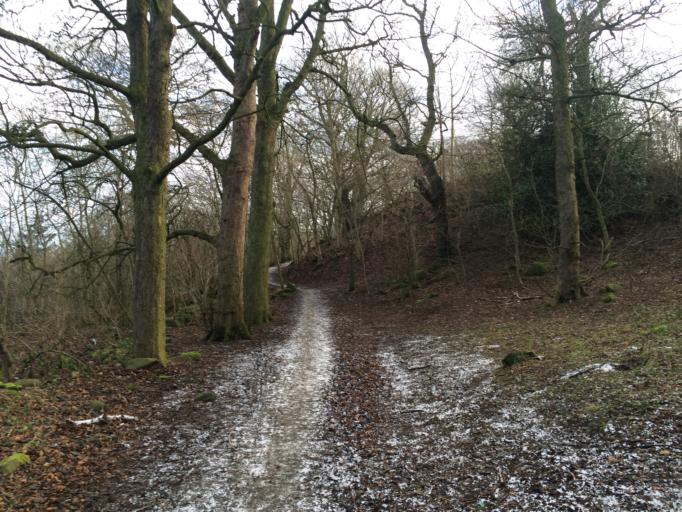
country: GB
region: Scotland
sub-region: Edinburgh
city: Colinton
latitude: 55.9490
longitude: -3.2686
